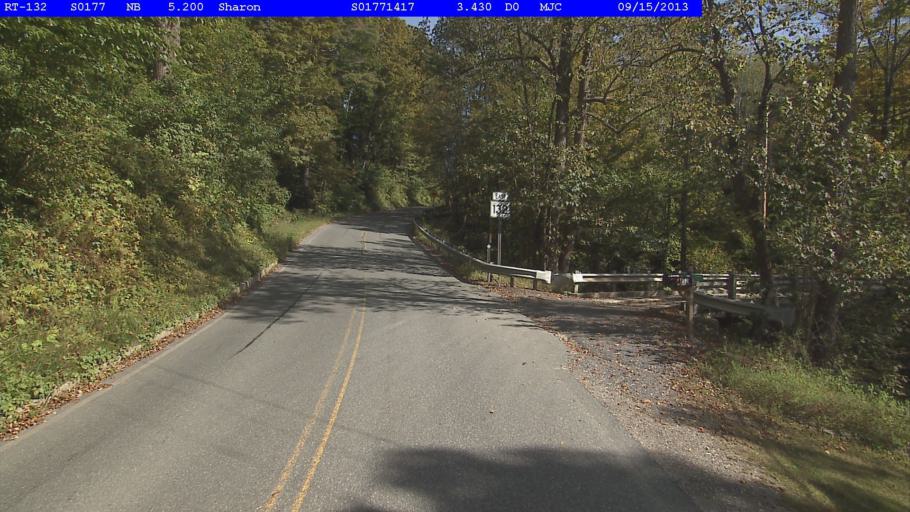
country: US
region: Vermont
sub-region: Windsor County
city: Woodstock
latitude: 43.7883
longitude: -72.4500
